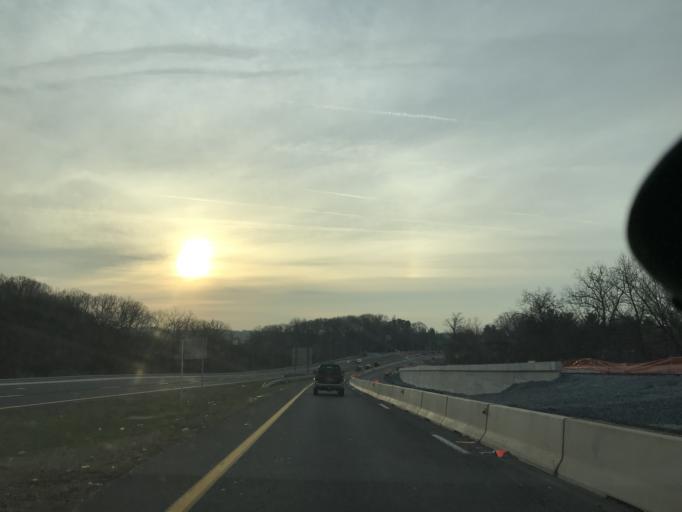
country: US
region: Maryland
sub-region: Prince George's County
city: Woodlawn
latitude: 38.9502
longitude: -76.8840
